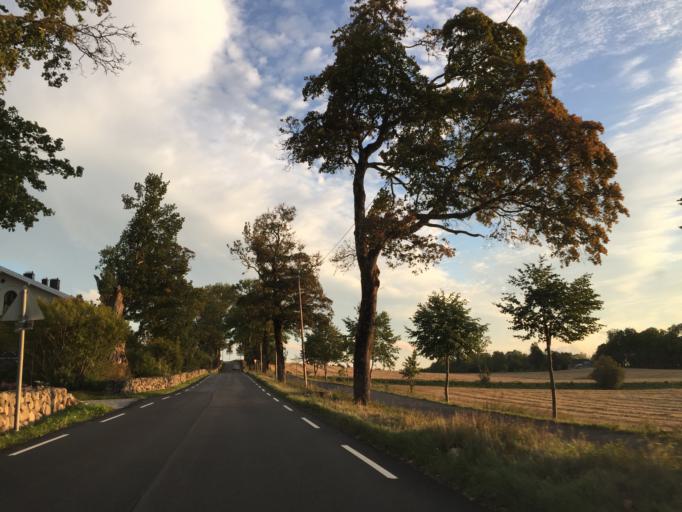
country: NO
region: Akershus
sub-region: As
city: As
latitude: 59.7167
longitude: 10.7758
